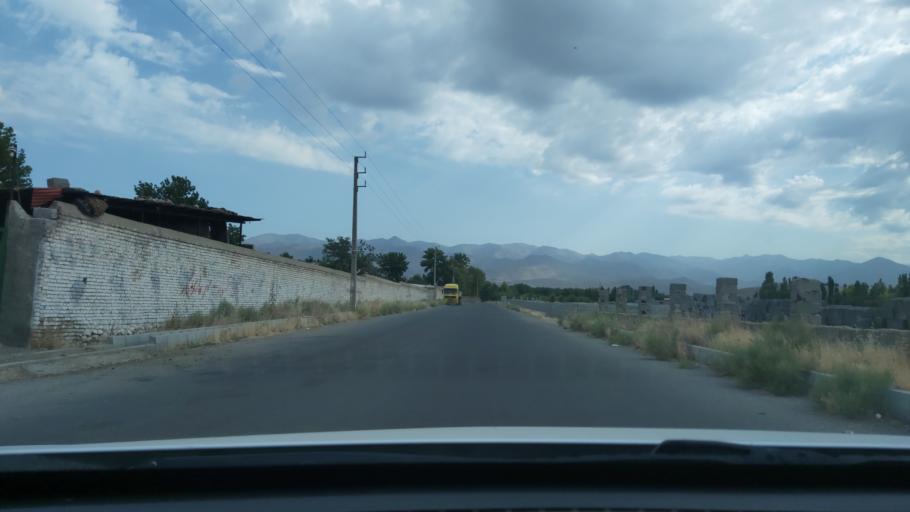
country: IR
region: Alborz
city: Hashtgerd
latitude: 35.9457
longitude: 50.7719
